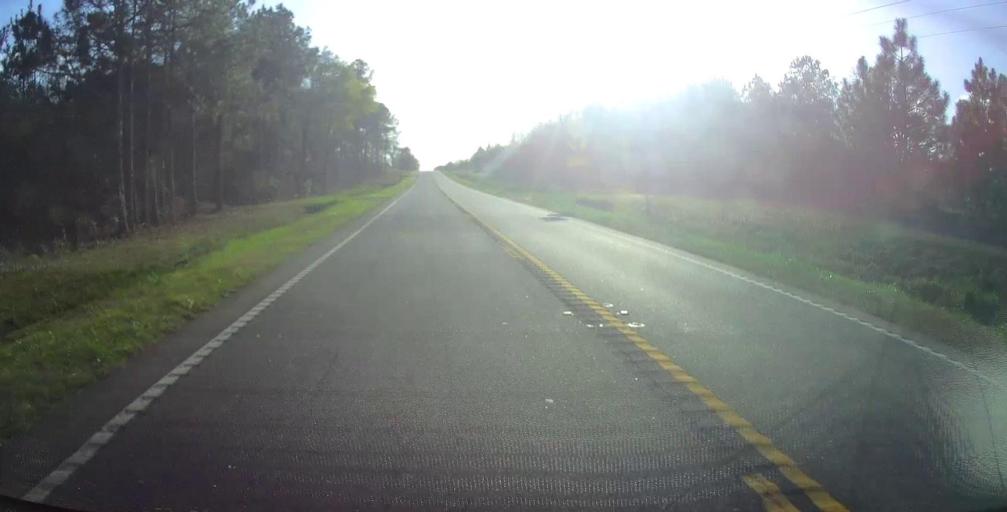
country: US
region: Georgia
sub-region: Tattnall County
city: Reidsville
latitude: 32.1176
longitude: -82.0726
